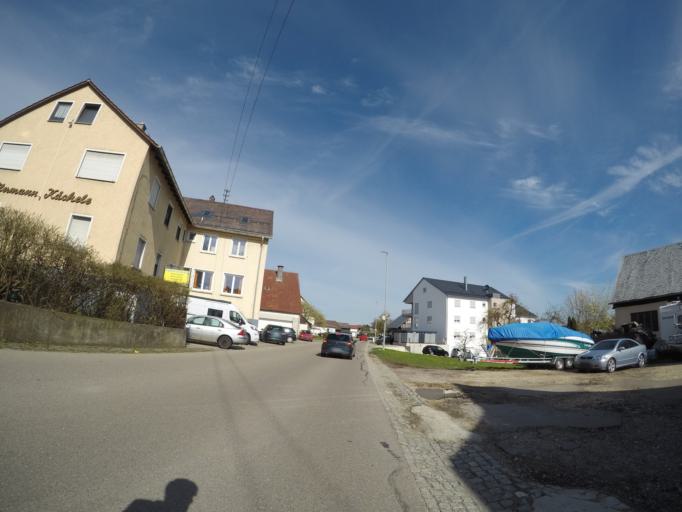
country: DE
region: Baden-Wuerttemberg
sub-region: Tuebingen Region
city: Laichingen
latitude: 48.4938
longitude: 9.6813
